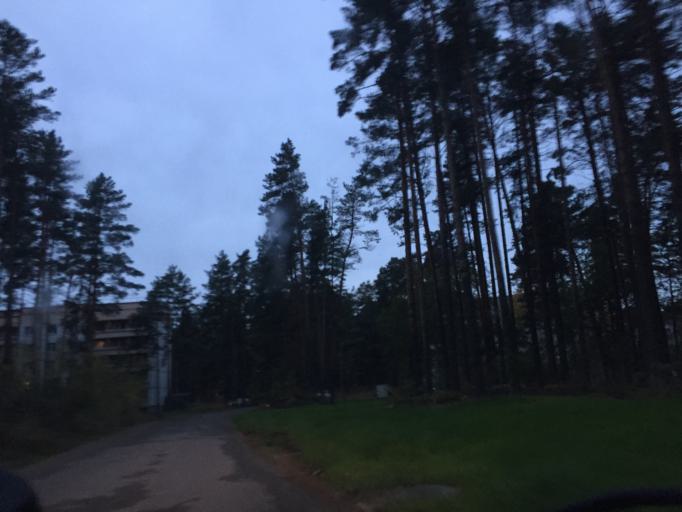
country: LV
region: Adazi
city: Adazi
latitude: 57.0897
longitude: 24.3622
